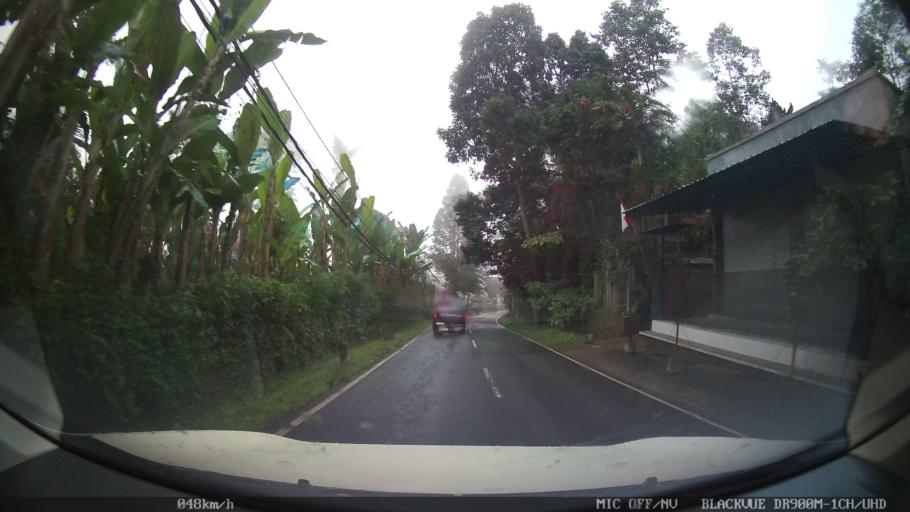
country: ID
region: Bali
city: Banjar Taro Kelod
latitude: -8.3470
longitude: 115.2791
